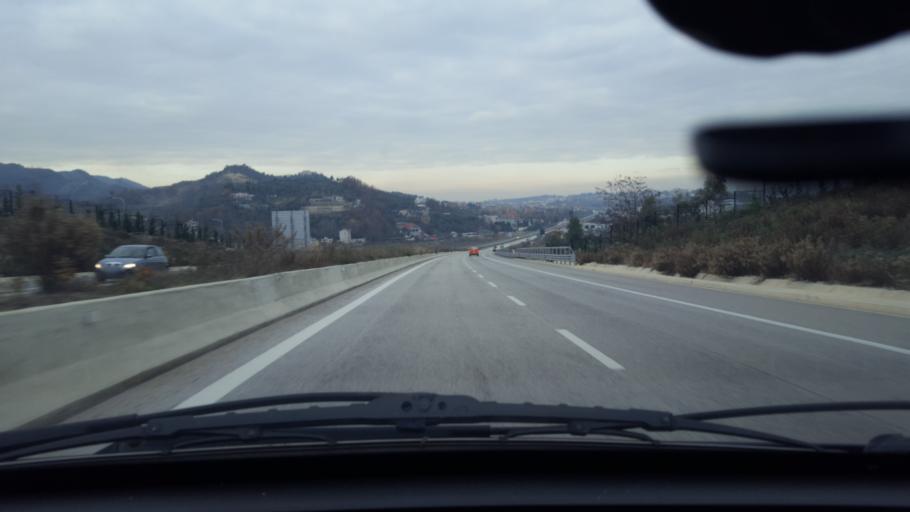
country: AL
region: Tirane
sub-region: Rrethi i Tiranes
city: Petrele
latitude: 41.2717
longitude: 19.8599
